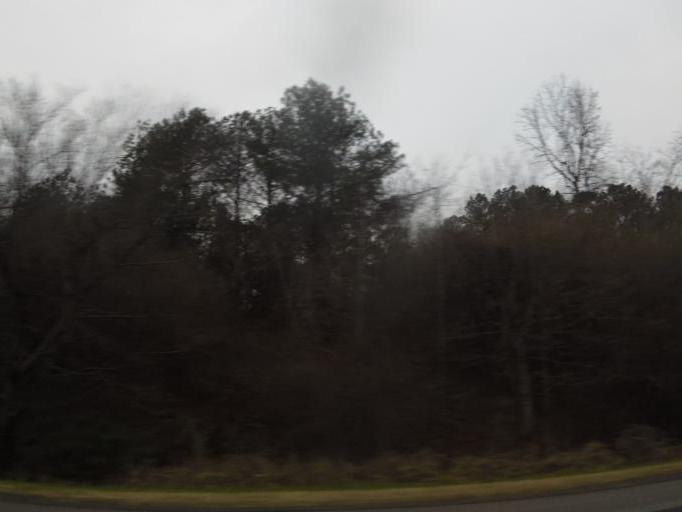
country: US
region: Alabama
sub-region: Jefferson County
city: Kimberly
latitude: 33.7664
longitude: -86.8306
